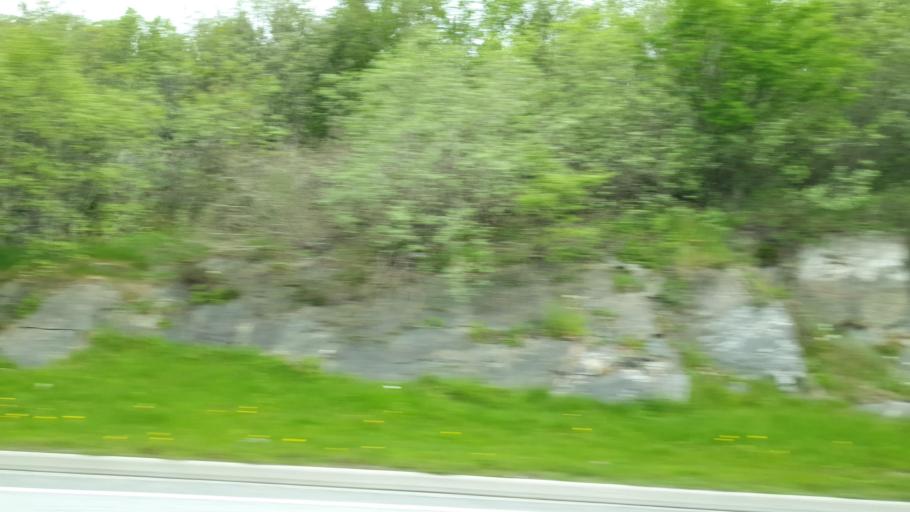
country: NO
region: More og Romsdal
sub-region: Alesund
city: Alesund
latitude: 62.4913
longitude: 6.1859
